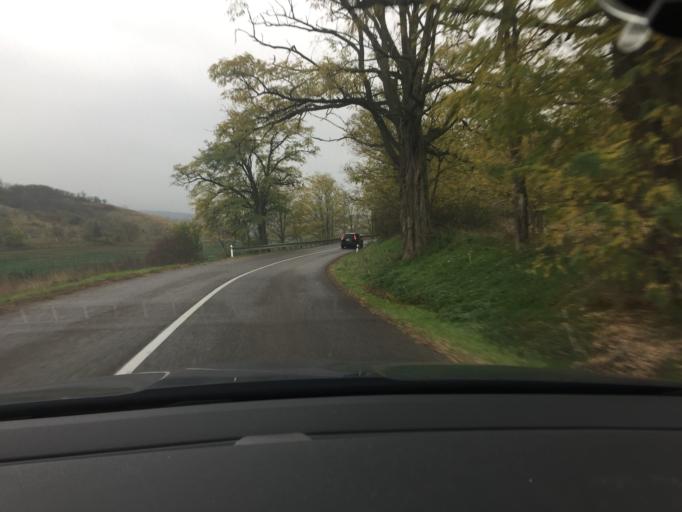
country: HU
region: Komarom-Esztergom
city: Esztergom
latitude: 47.8663
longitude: 18.7514
